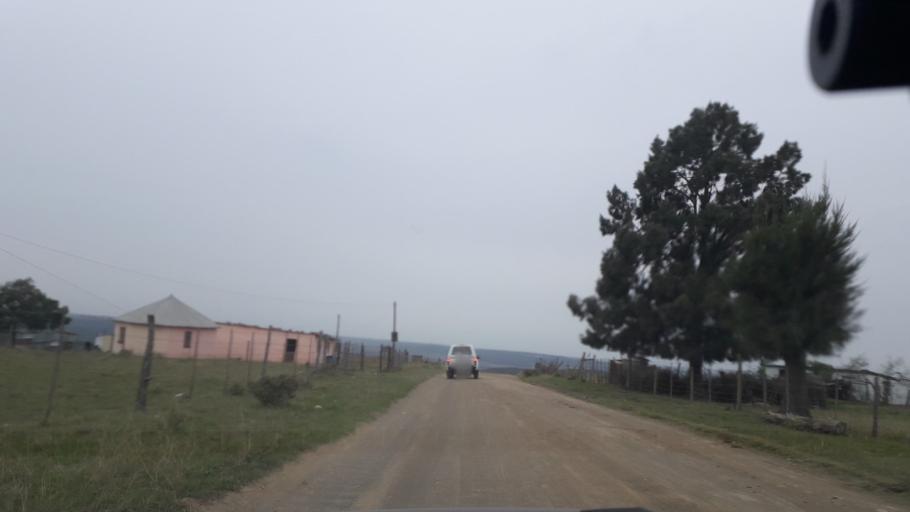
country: ZA
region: Eastern Cape
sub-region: Buffalo City Metropolitan Municipality
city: Bhisho
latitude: -32.7893
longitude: 27.3249
